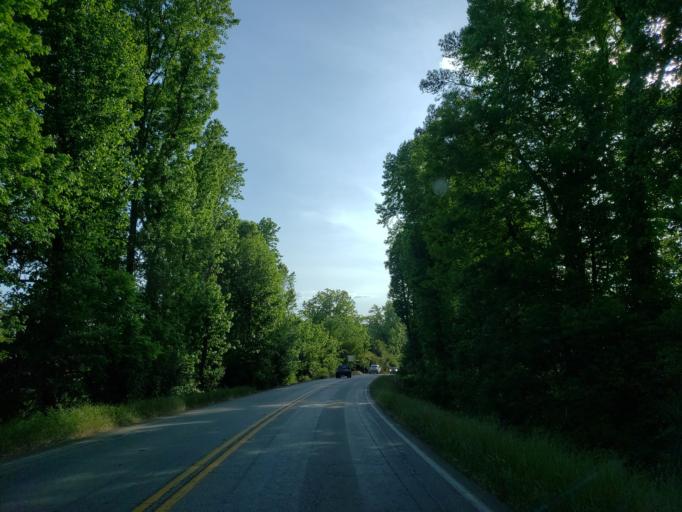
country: US
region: Georgia
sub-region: Carroll County
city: Bowdon
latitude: 33.4667
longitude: -85.2994
